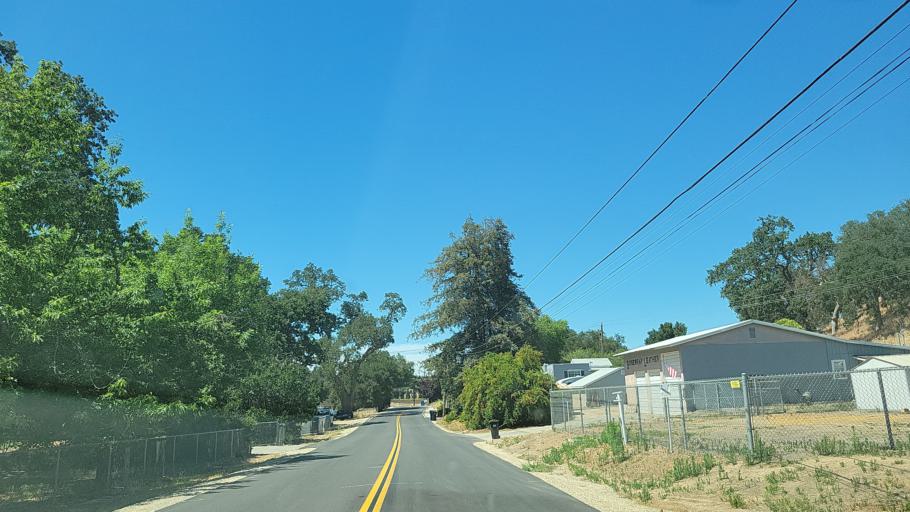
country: US
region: California
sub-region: San Luis Obispo County
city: Atascadero
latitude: 35.4931
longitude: -120.6444
